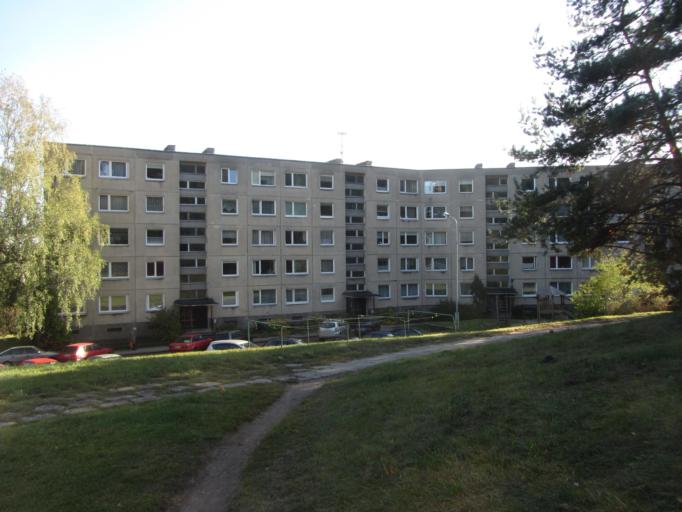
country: LT
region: Vilnius County
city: Lazdynai
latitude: 54.6814
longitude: 25.2158
